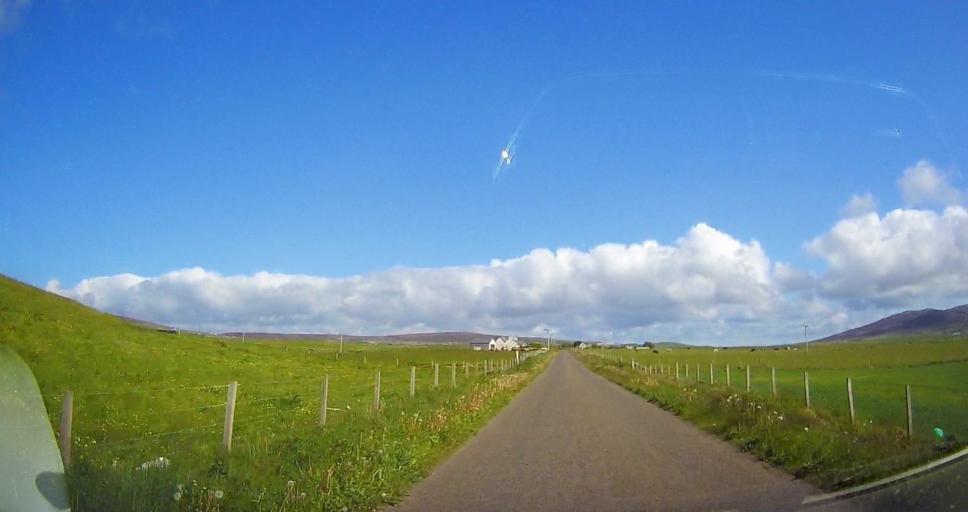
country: GB
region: Scotland
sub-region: Orkney Islands
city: Stromness
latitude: 58.9980
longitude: -3.1672
